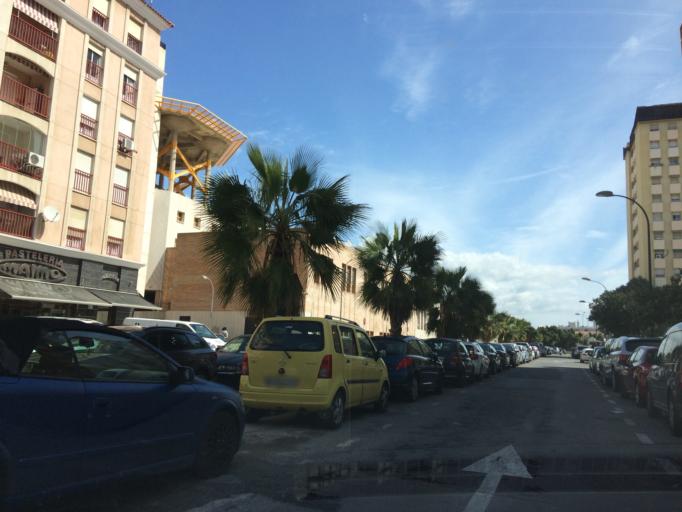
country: ES
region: Andalusia
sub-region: Provincia de Malaga
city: Malaga
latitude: 36.7135
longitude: -4.4496
